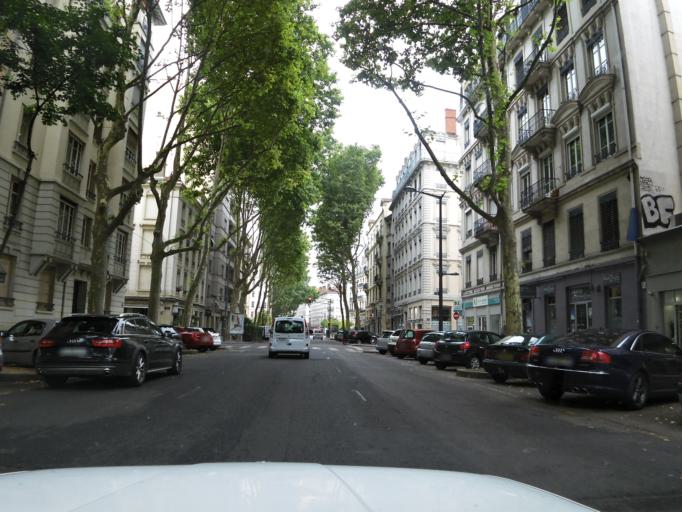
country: FR
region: Rhone-Alpes
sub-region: Departement du Rhone
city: Lyon
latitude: 45.7684
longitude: 4.8569
